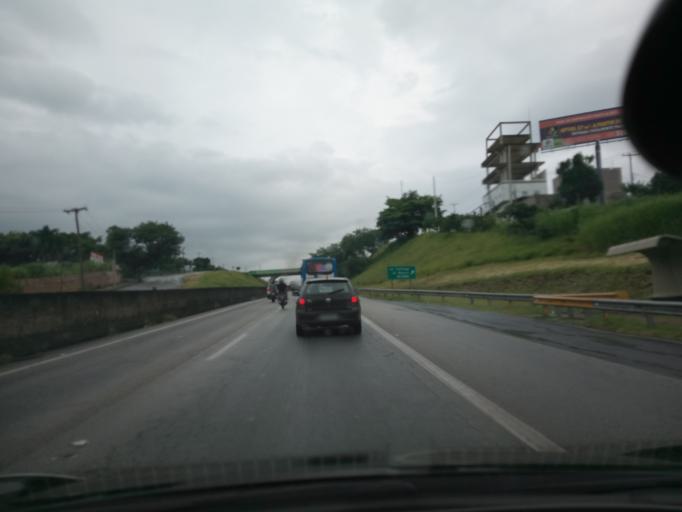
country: BR
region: Sao Paulo
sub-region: Campinas
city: Campinas
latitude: -22.9709
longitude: -47.1019
